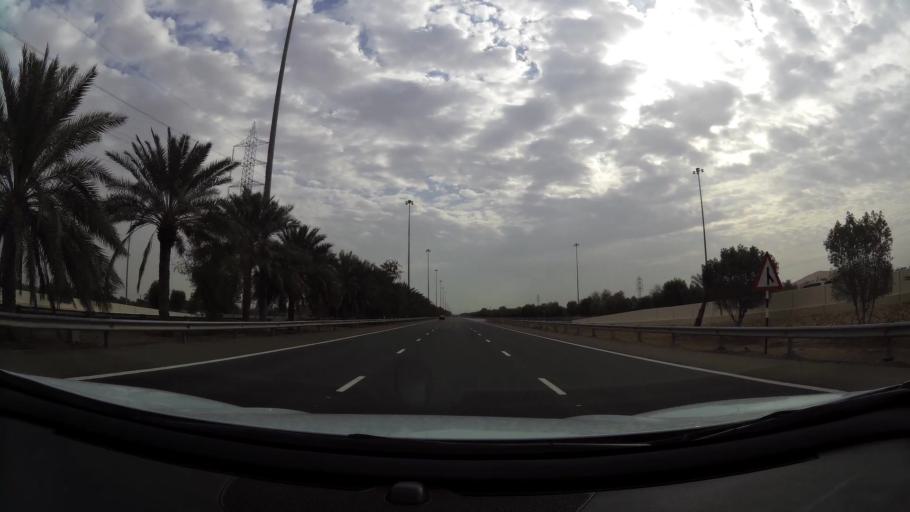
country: AE
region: Abu Dhabi
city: Al Ain
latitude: 24.2110
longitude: 55.4671
